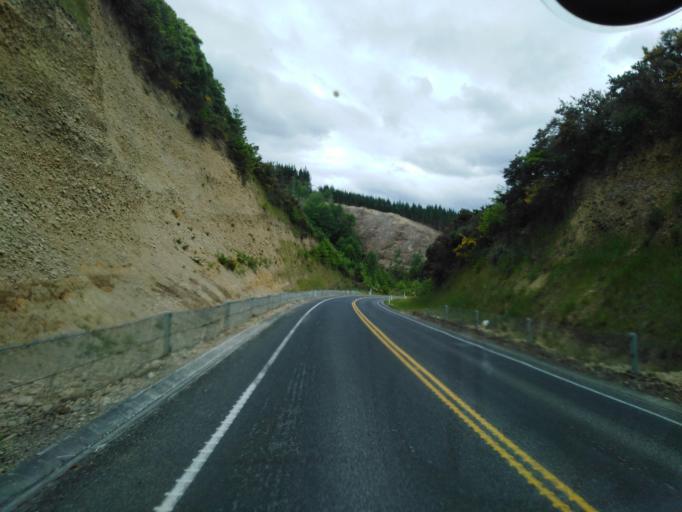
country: NZ
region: Tasman
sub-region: Tasman District
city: Wakefield
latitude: -41.4822
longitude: 172.9065
